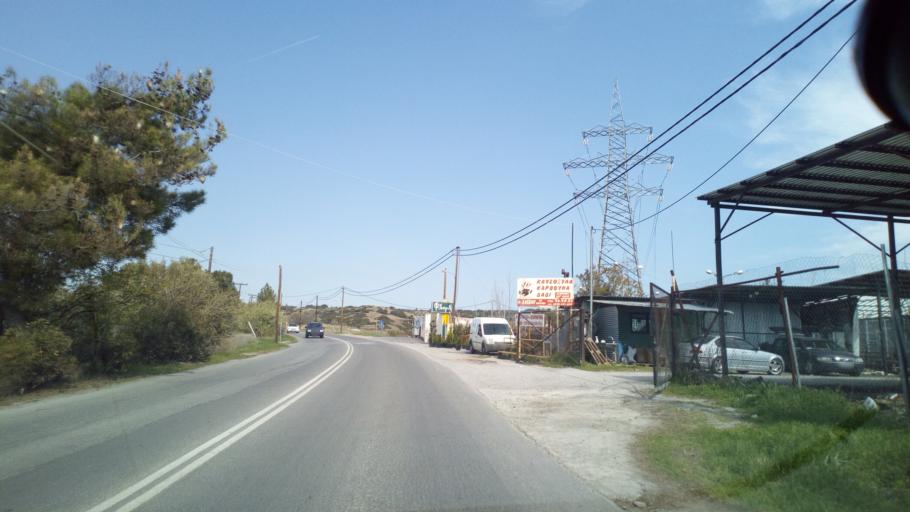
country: GR
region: Central Macedonia
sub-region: Nomos Thessalonikis
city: Thermi
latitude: 40.5631
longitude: 23.0242
